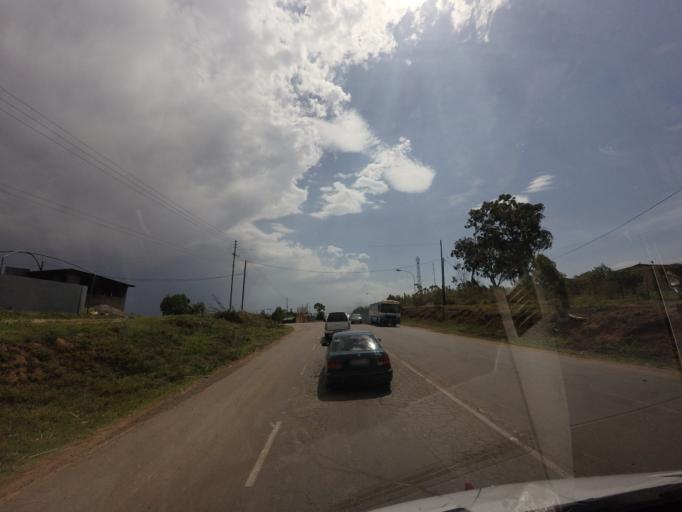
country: SZ
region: Manzini
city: Manzini
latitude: -26.4934
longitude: 31.4050
